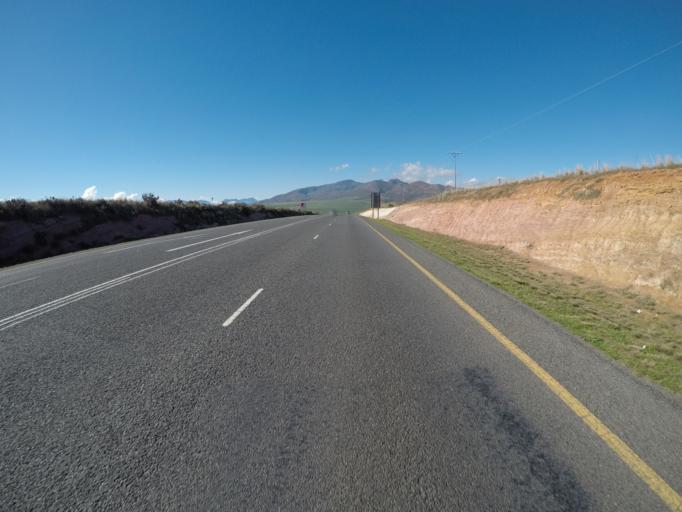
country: ZA
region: Western Cape
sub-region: Overberg District Municipality
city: Caledon
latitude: -34.2099
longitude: 19.3831
